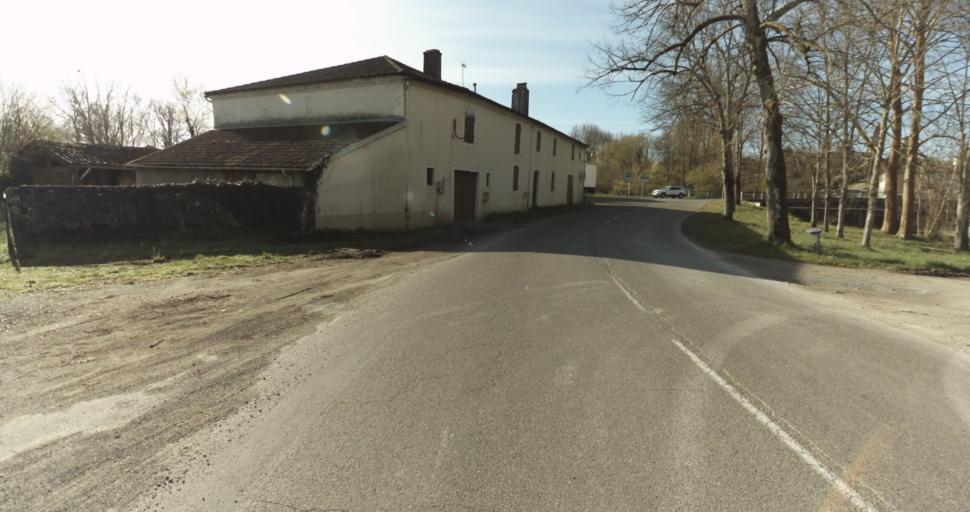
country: FR
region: Aquitaine
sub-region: Departement des Landes
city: Sarbazan
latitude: 43.9848
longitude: -0.2277
